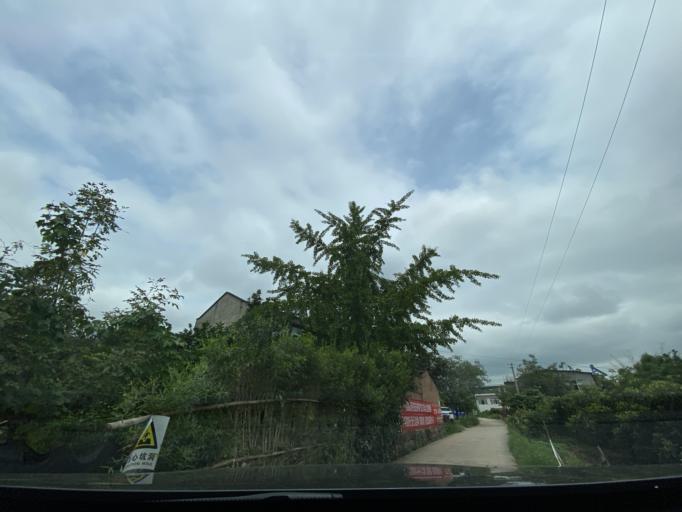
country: CN
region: Sichuan
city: Jiancheng
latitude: 30.4018
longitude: 104.5684
